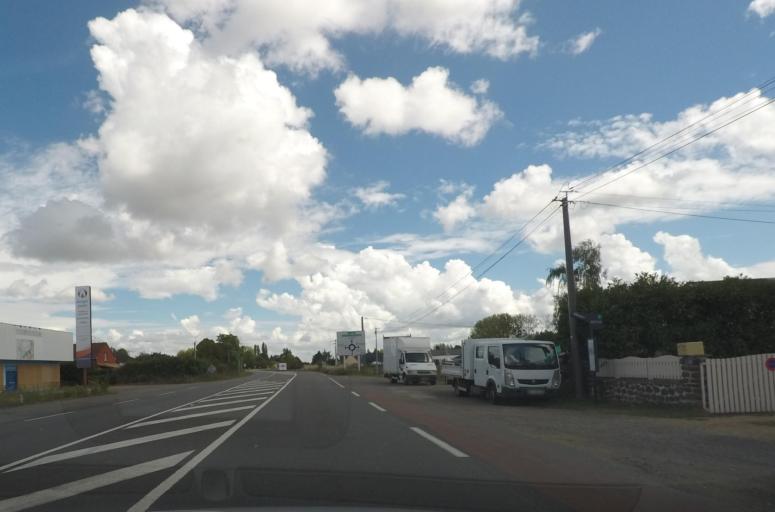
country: FR
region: Pays de la Loire
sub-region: Departement de la Sarthe
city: Spay
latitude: 47.9003
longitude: 0.1588
